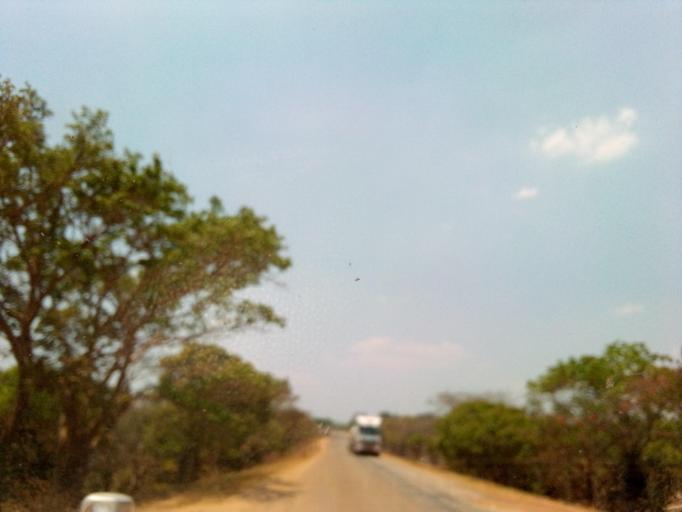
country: ZM
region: Northern
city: Mpika
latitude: -12.2092
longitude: 31.1791
